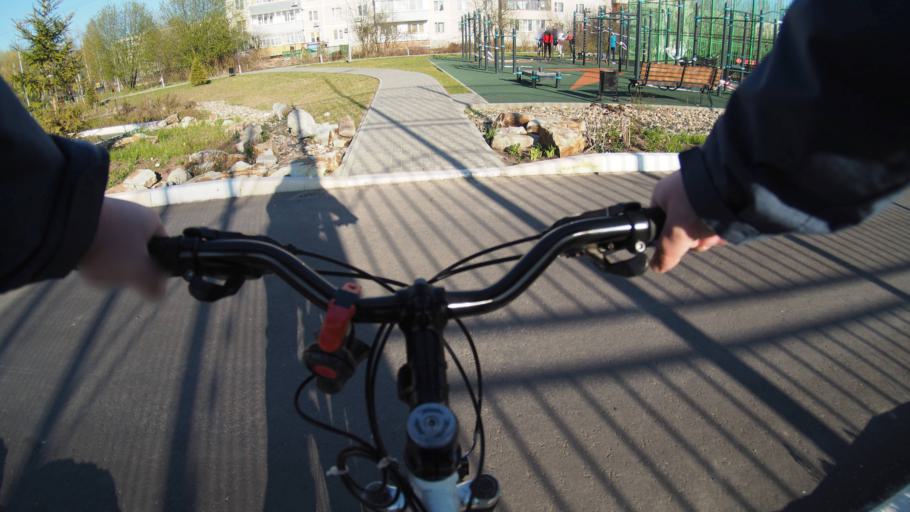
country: RU
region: Moskovskaya
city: Malyshevo
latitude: 55.5080
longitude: 38.3377
